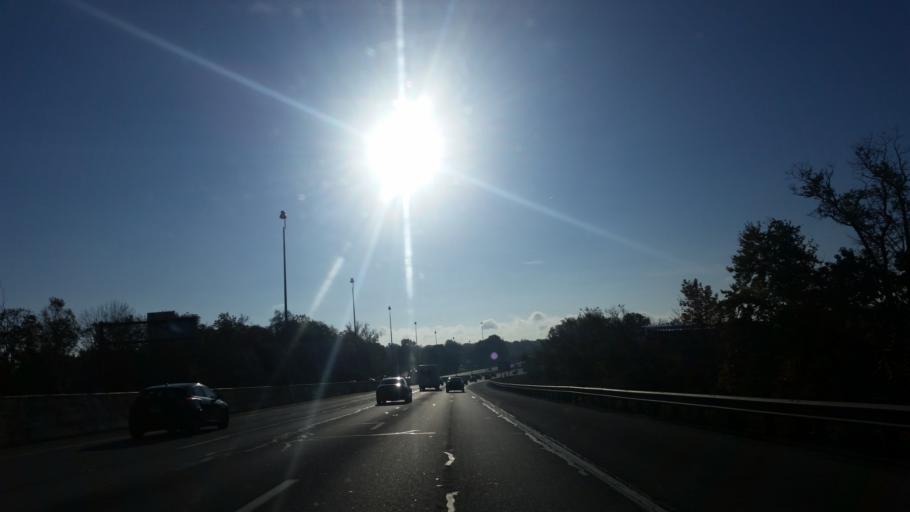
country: US
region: Ohio
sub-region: Summit County
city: Fairlawn
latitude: 41.1041
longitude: -81.5943
